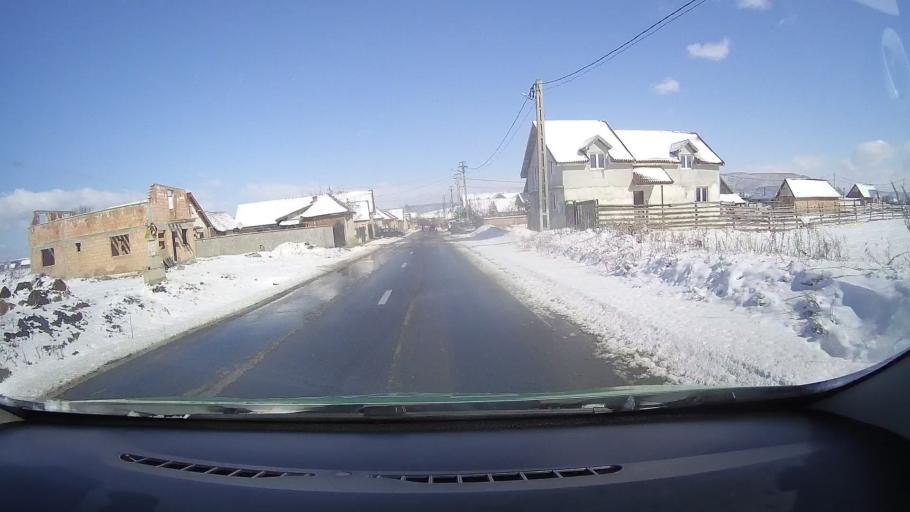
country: RO
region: Sibiu
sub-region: Comuna Rosia
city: Rosia
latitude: 45.8145
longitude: 24.3077
